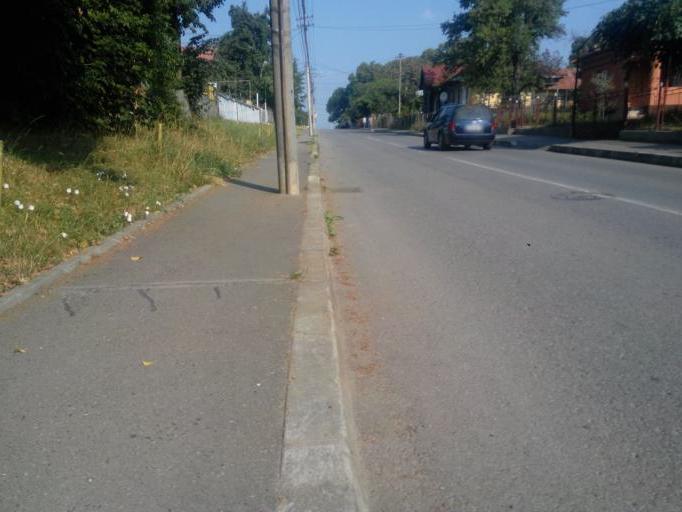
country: RO
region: Suceava
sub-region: Municipiul Falticeni
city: Falticeni
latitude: 47.4648
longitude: 26.2888
